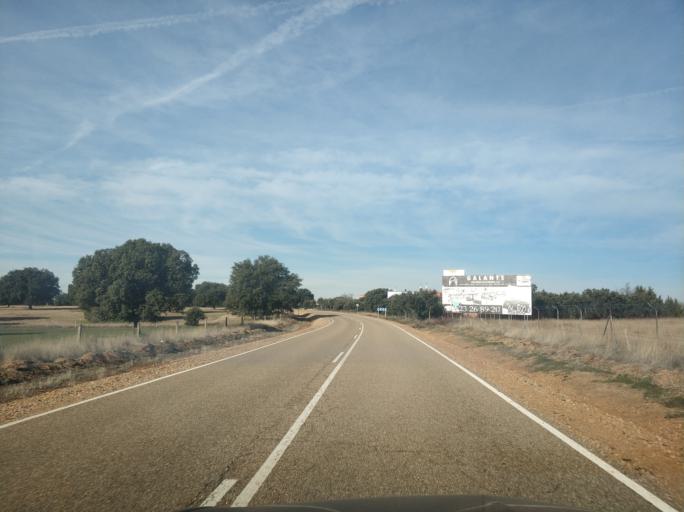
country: ES
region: Castille and Leon
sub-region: Provincia de Salamanca
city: Zarapicos
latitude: 41.0082
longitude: -5.8430
